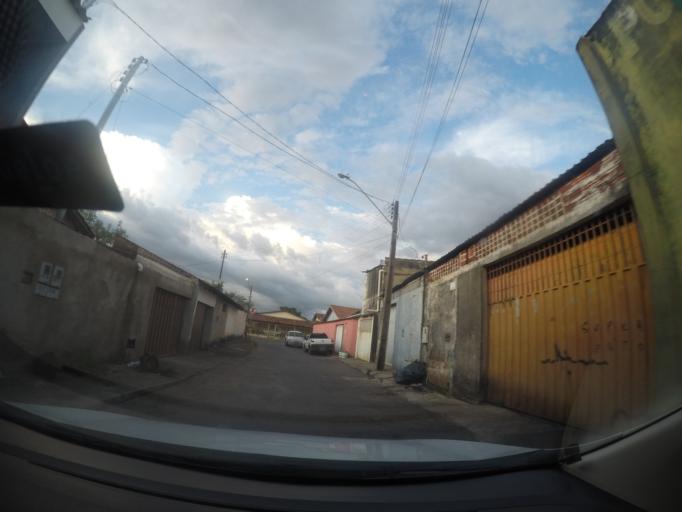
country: BR
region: Goias
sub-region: Goiania
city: Goiania
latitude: -16.6917
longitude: -49.3177
